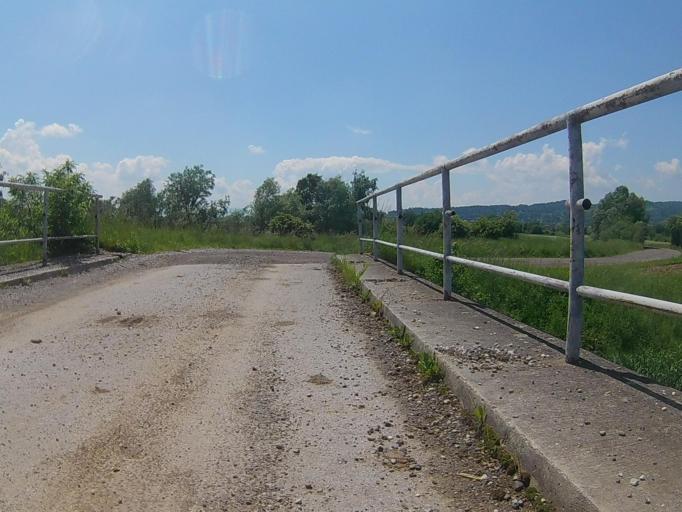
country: SI
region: Hoce-Slivnica
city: Radizel
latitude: 46.4862
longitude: 15.6673
